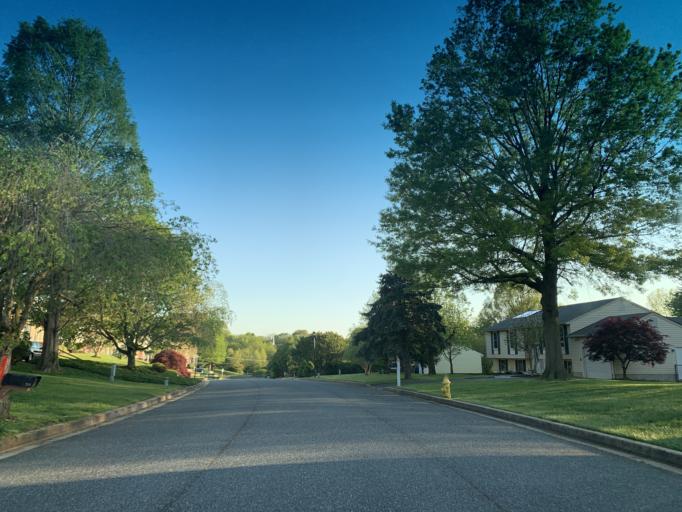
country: US
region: Maryland
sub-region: Harford County
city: Aberdeen
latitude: 39.5216
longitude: -76.1627
